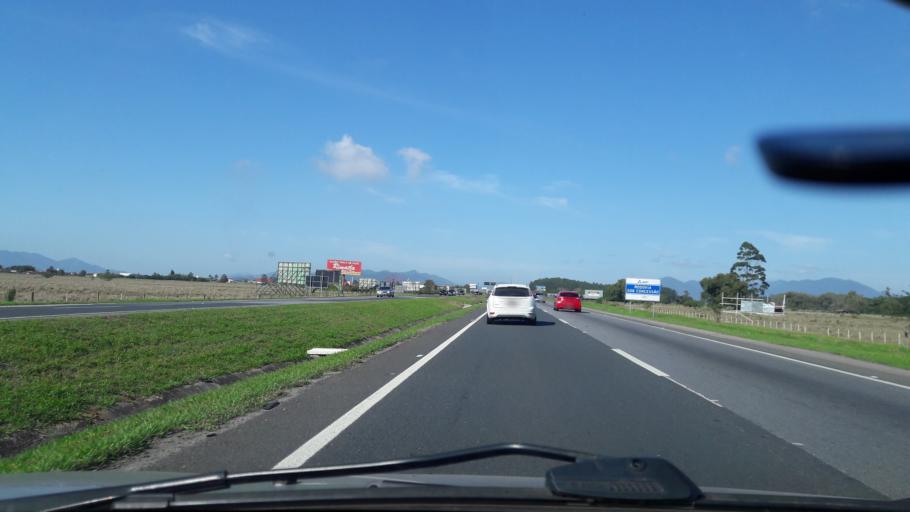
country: BR
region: Santa Catarina
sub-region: Tijucas
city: Tijucas
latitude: -27.2009
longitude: -48.6158
